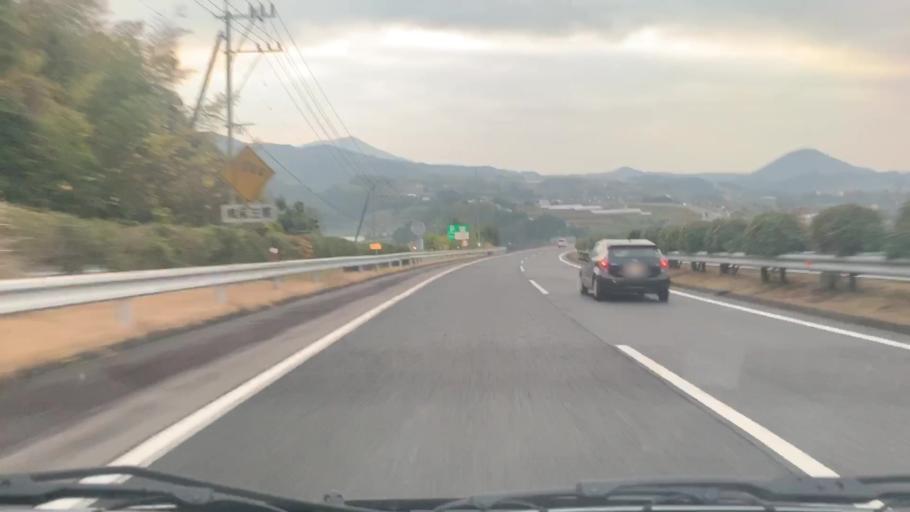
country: JP
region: Nagasaki
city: Omura
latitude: 33.0258
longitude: 129.9391
